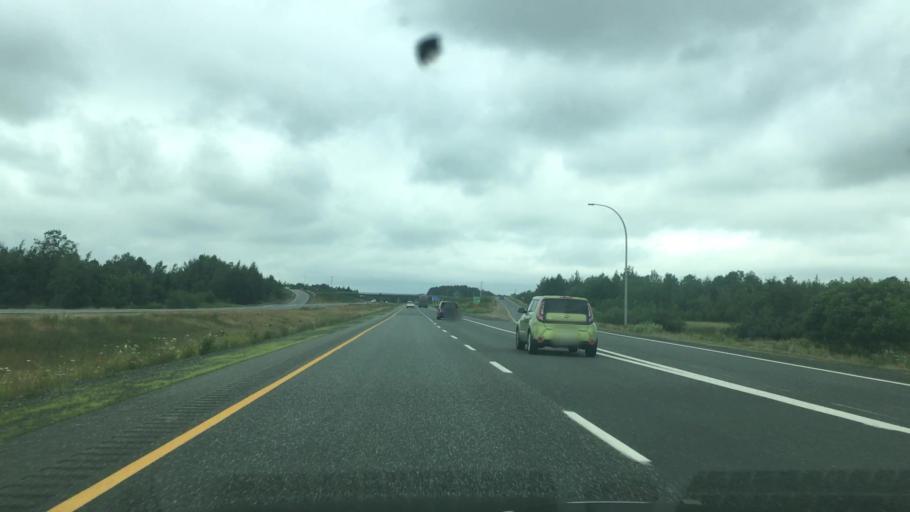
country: CA
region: Nova Scotia
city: Truro
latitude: 45.3960
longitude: -63.4211
